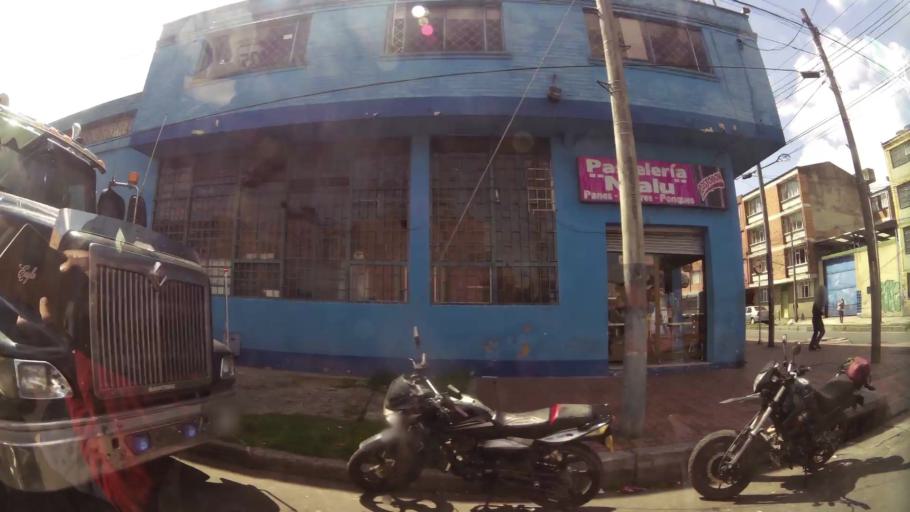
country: CO
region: Bogota D.C.
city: Bogota
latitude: 4.6210
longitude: -74.0799
